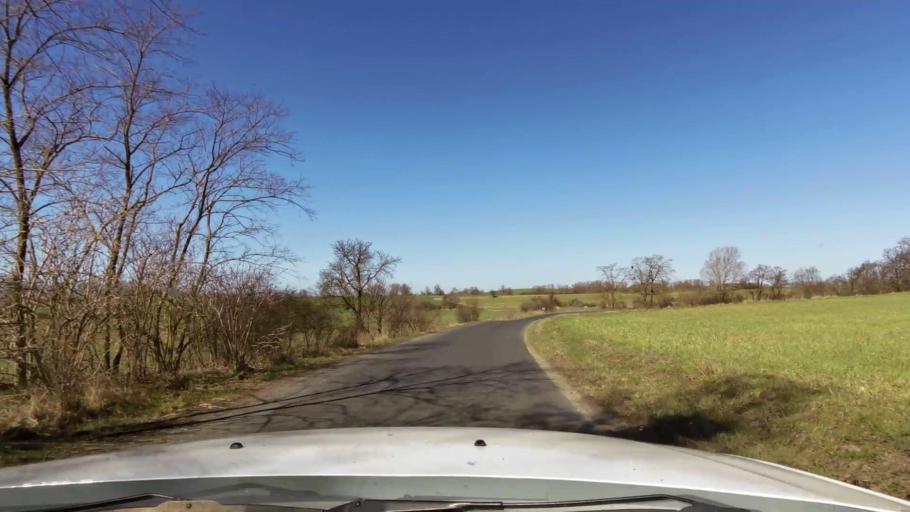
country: PL
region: West Pomeranian Voivodeship
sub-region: Powiat gryfinski
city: Cedynia
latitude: 52.8573
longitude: 14.2865
